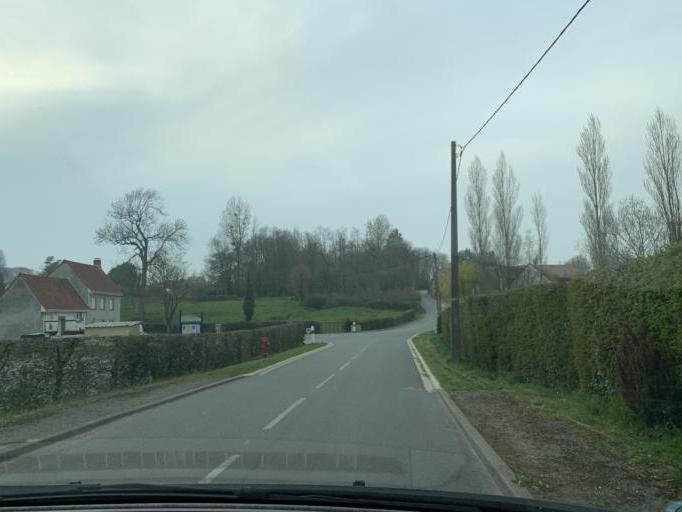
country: FR
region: Nord-Pas-de-Calais
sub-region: Departement du Pas-de-Calais
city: Samer
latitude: 50.6636
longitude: 1.7510
